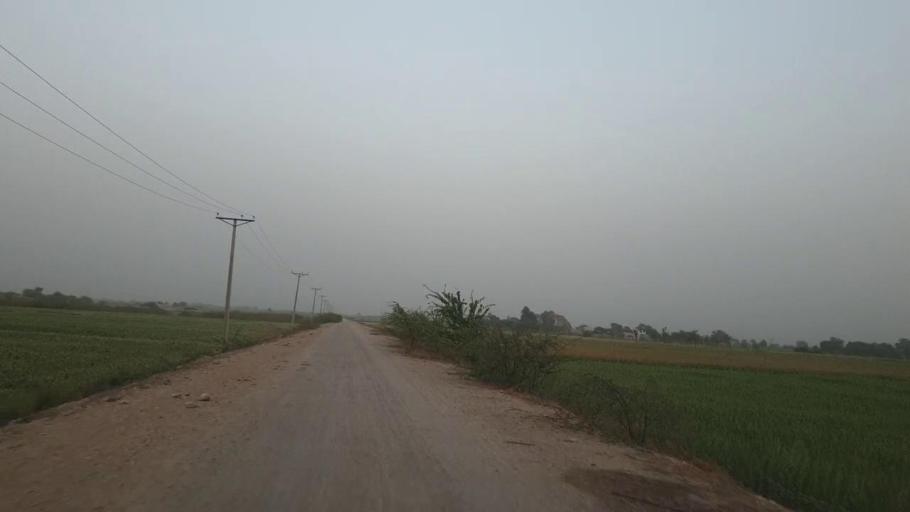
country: PK
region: Sindh
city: Kunri
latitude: 25.1221
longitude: 69.5724
